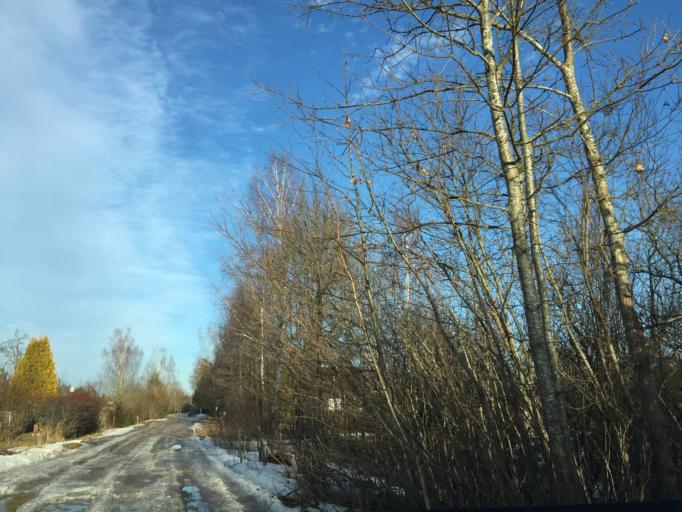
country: LV
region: Lecava
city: Iecava
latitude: 56.6914
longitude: 24.0776
